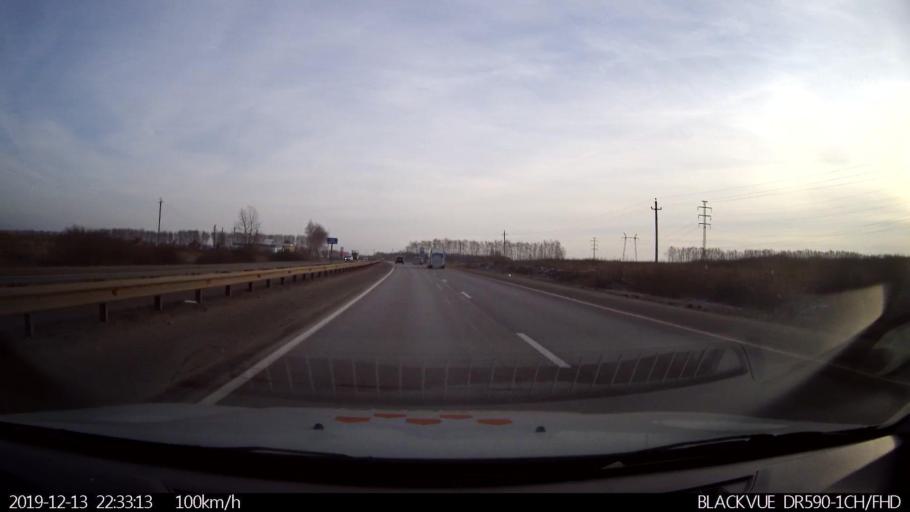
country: RU
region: Nizjnij Novgorod
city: Afonino
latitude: 56.1987
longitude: 44.1082
